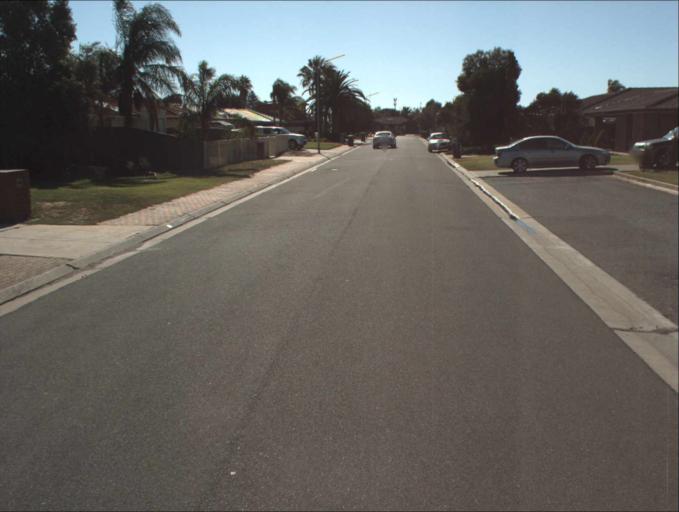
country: AU
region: South Australia
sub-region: Port Adelaide Enfield
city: Birkenhead
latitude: -34.7826
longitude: 138.4954
